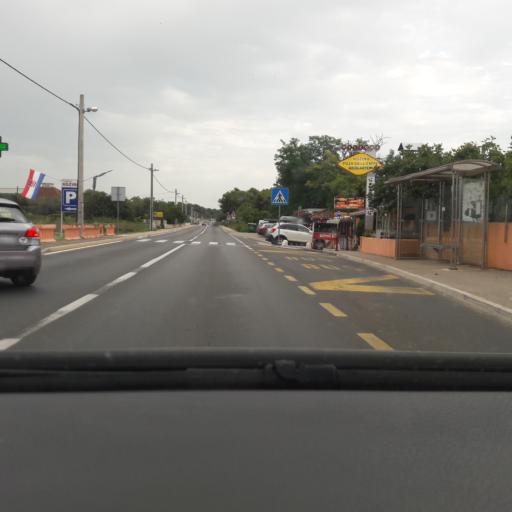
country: HR
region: Zadarska
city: Nin
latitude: 44.1705
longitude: 15.1950
